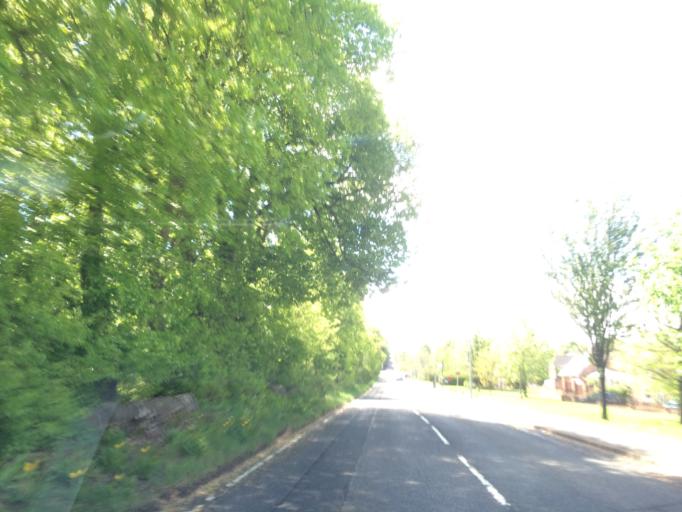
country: GB
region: Scotland
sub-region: East Renfrewshire
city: Newton Mearns
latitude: 55.7969
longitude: -4.3278
